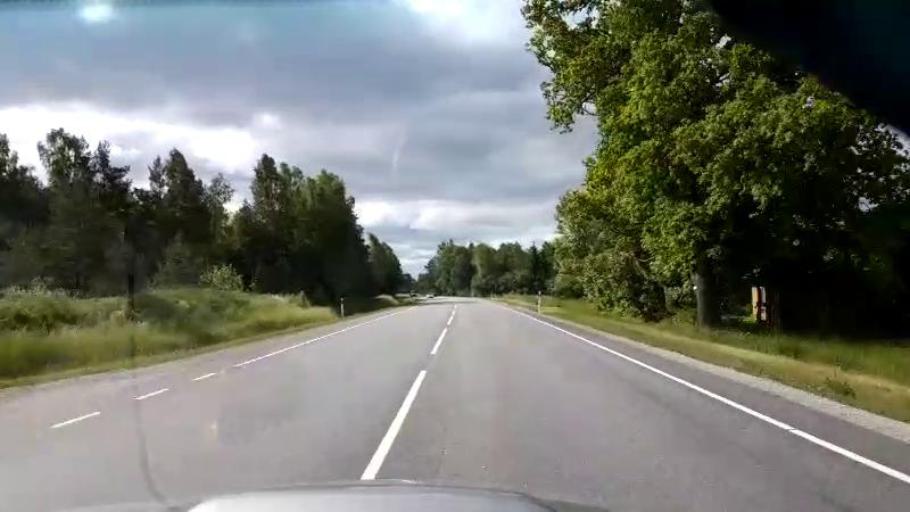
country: EE
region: Raplamaa
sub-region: Maerjamaa vald
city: Marjamaa
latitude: 58.9681
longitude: 24.4764
